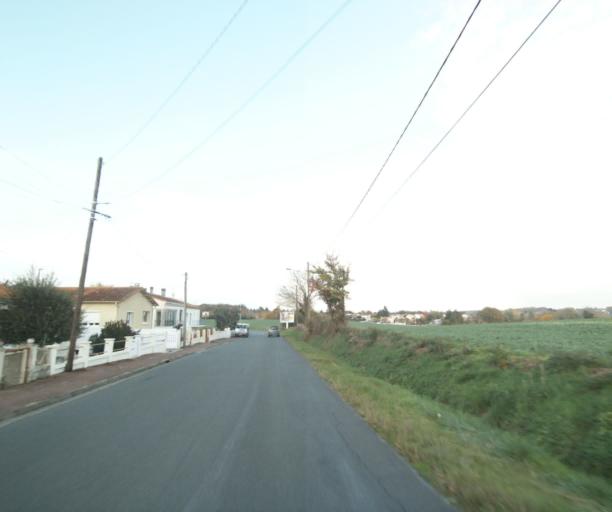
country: FR
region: Poitou-Charentes
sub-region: Departement de la Charente-Maritime
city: Saintes
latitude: 45.7564
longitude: -0.6389
